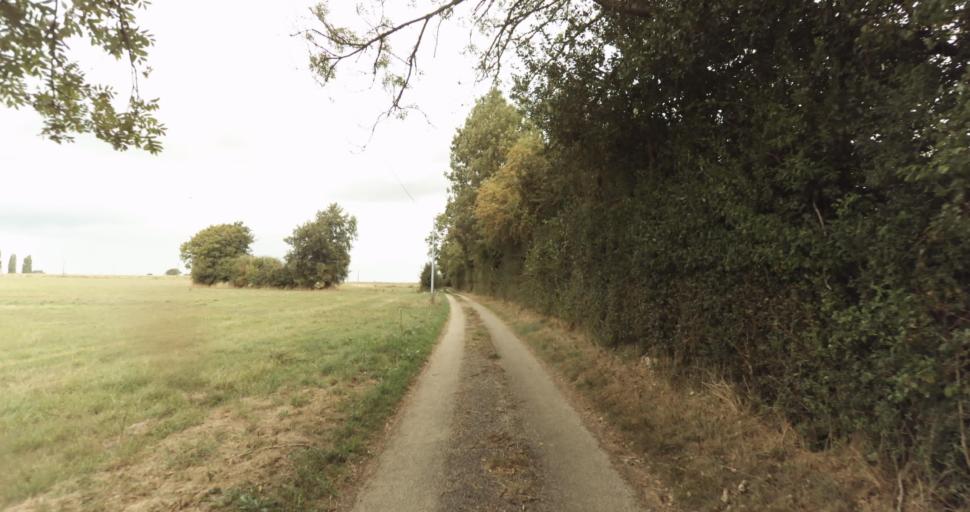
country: FR
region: Lower Normandy
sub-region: Departement du Calvados
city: Orbec
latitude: 48.9107
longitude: 0.3724
